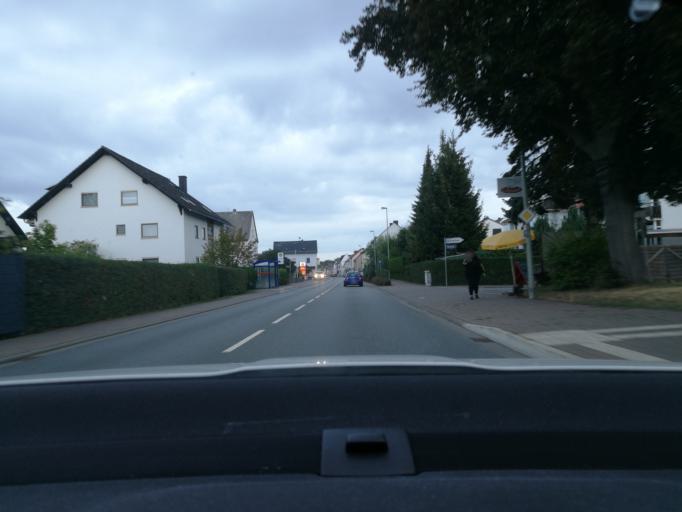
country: DE
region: Rheinland-Pfalz
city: Holzheim
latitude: 50.3663
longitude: 8.0926
